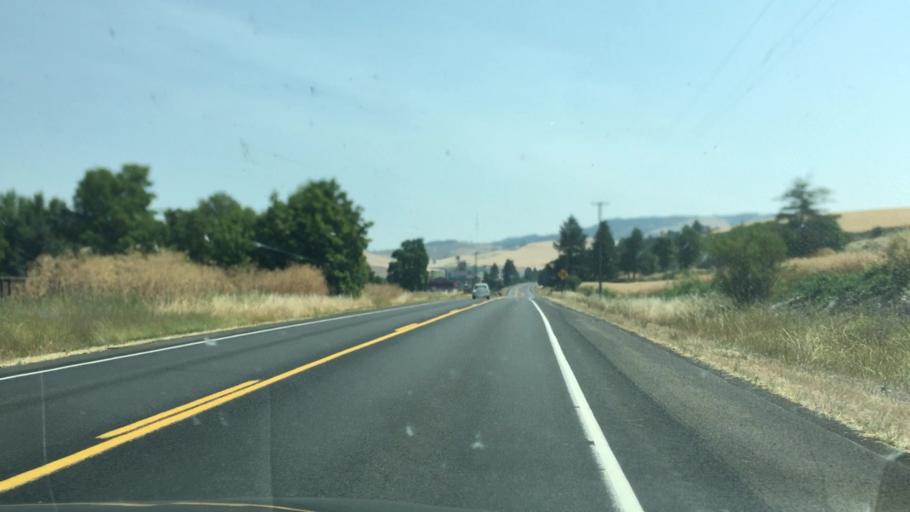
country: US
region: Idaho
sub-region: Nez Perce County
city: Lapwai
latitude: 46.3729
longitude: -116.6894
